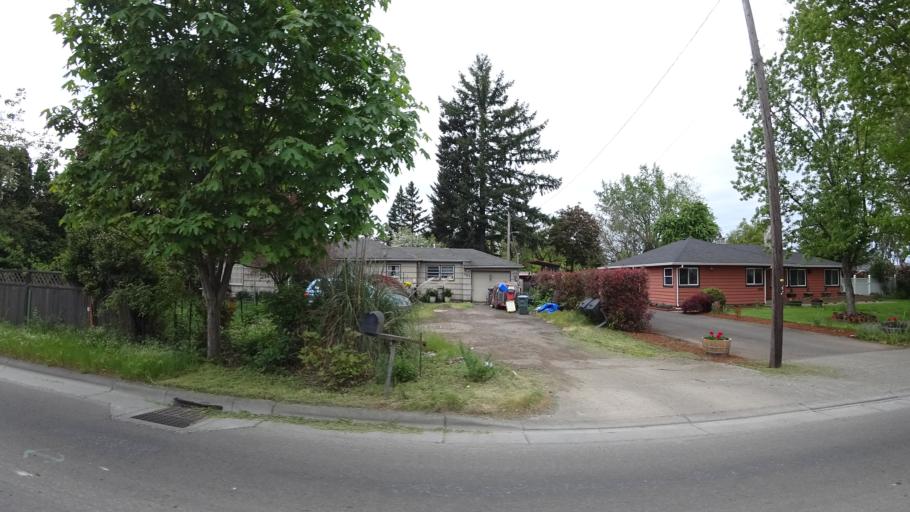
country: US
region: Oregon
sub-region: Washington County
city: Hillsboro
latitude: 45.4972
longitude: -122.9677
